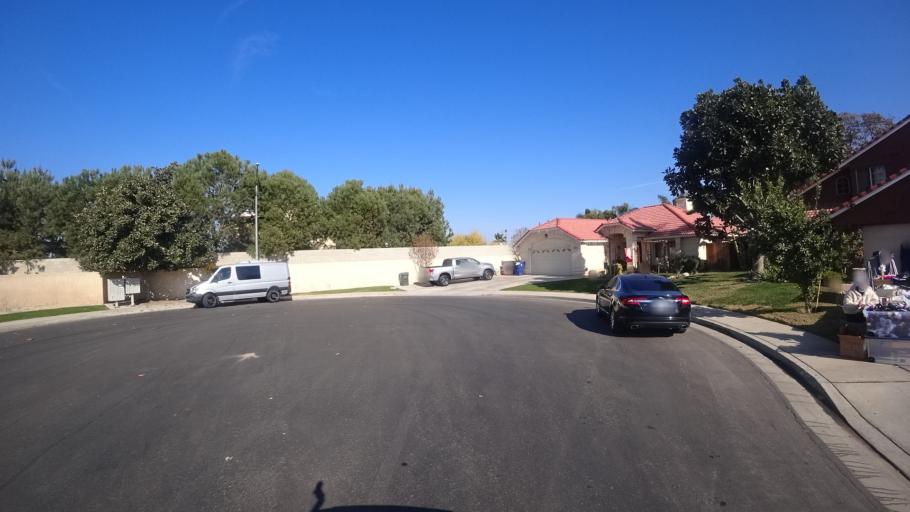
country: US
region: California
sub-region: Kern County
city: Greenacres
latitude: 35.3221
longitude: -119.1266
